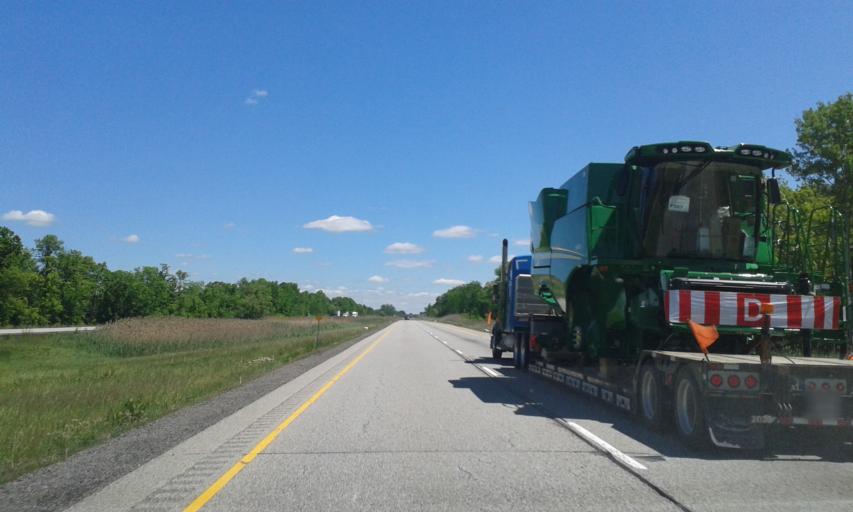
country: US
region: New York
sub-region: St. Lawrence County
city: Norfolk
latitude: 44.9309
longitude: -75.1646
